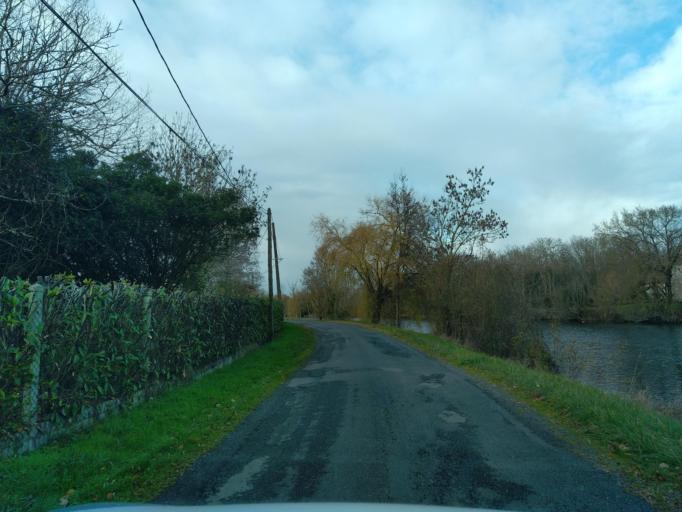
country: FR
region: Pays de la Loire
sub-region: Departement de la Vendee
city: Vix
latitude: 46.3333
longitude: -0.8083
